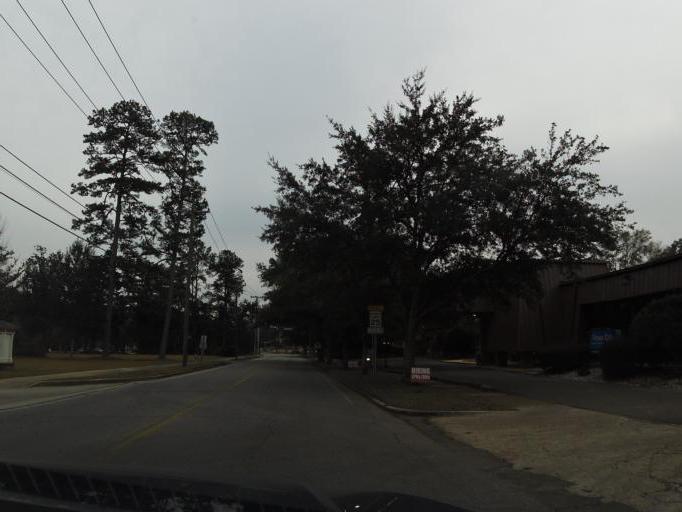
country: US
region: Georgia
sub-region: Thomas County
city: Thomasville
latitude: 30.8277
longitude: -83.9711
